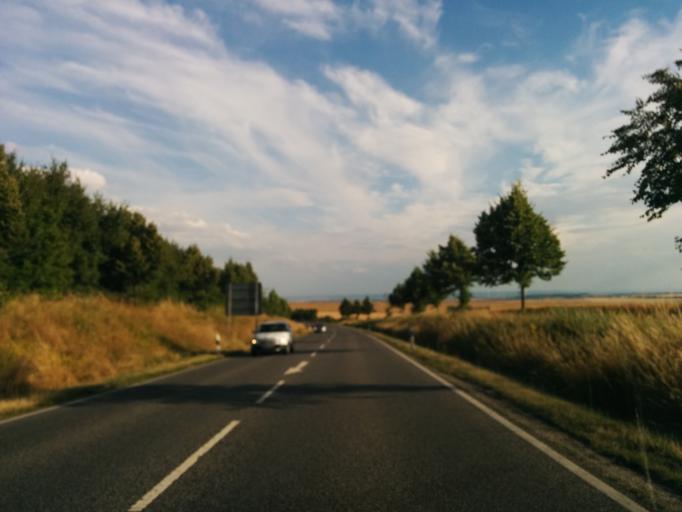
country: DE
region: Thuringia
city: Wasserthaleben
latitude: 51.2875
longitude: 10.8990
